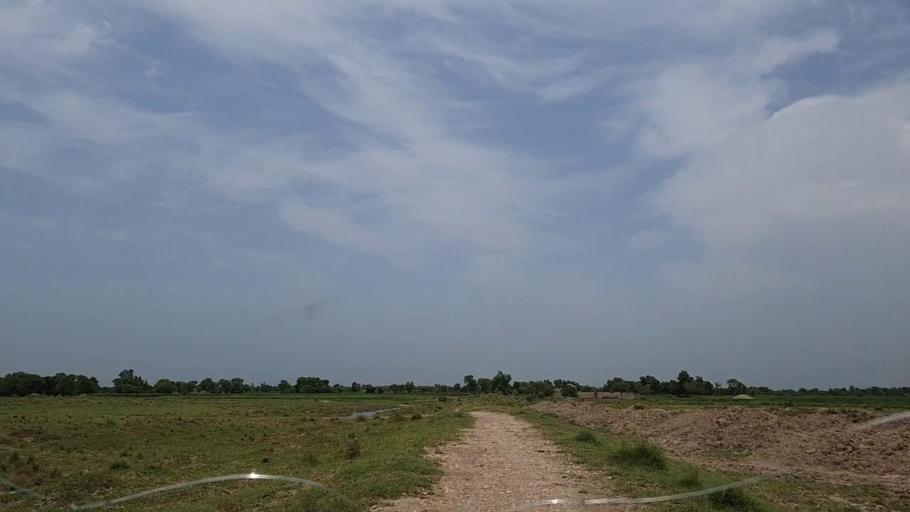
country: PK
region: Sindh
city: Tharu Shah
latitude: 26.9026
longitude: 68.0554
